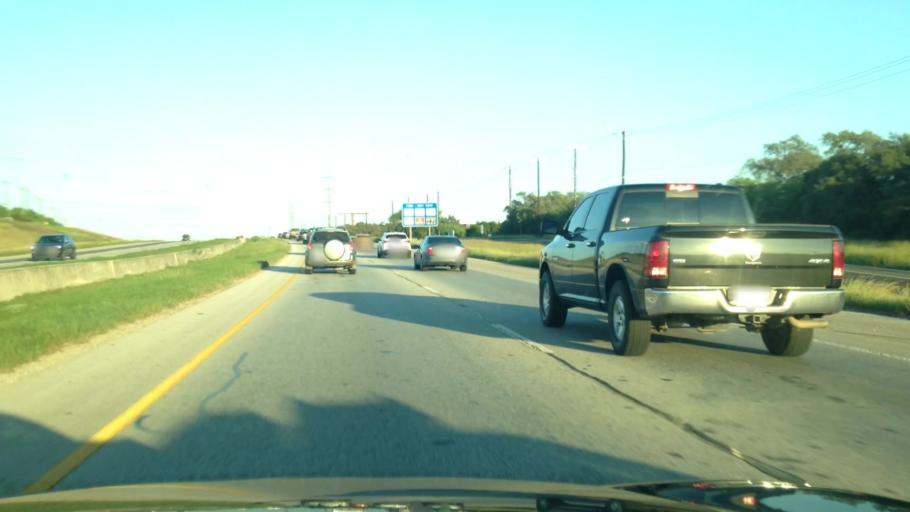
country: US
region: Texas
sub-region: Bexar County
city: Hollywood Park
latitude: 29.6001
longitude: -98.4326
